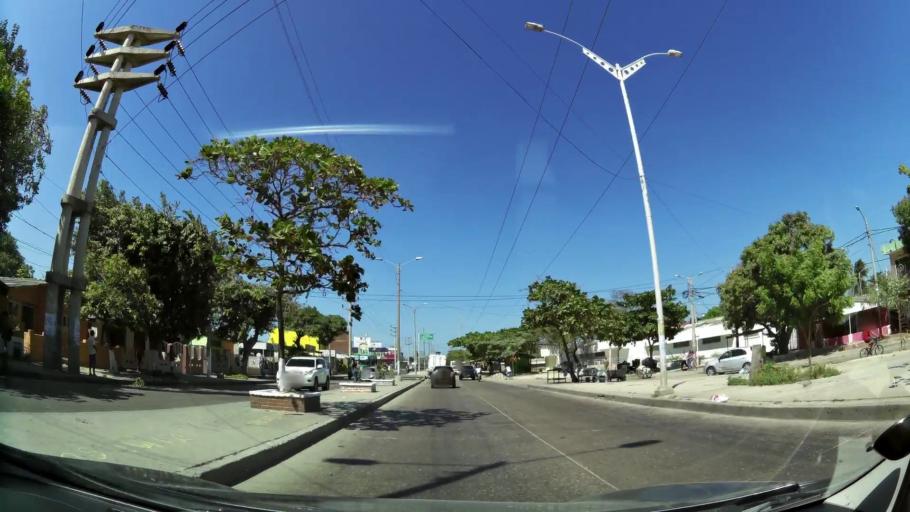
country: CO
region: Atlantico
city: Barranquilla
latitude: 10.9510
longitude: -74.7738
